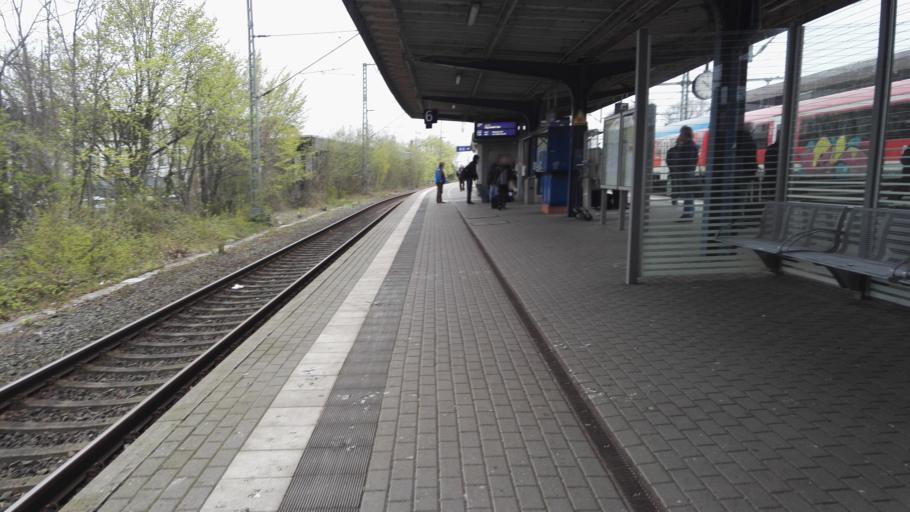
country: DE
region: Schleswig-Holstein
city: Neumunster
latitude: 54.0759
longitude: 9.9796
